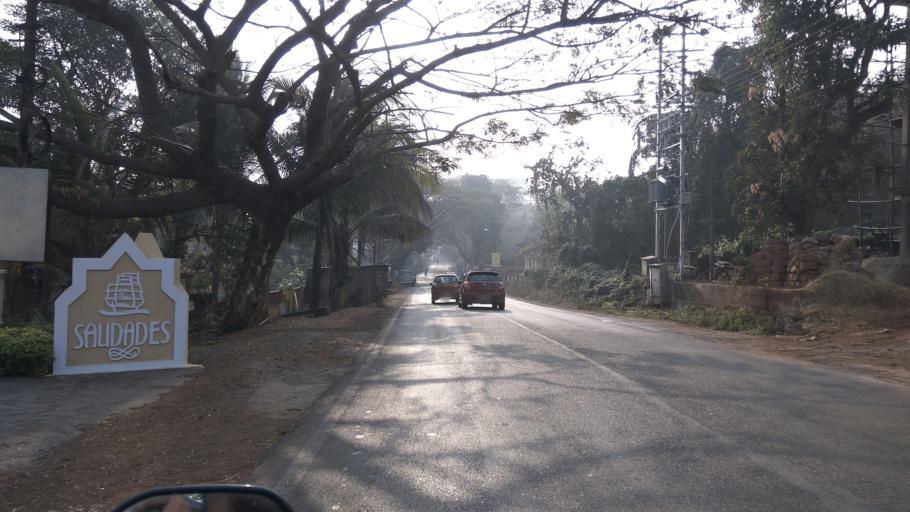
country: IN
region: Goa
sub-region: North Goa
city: Saligao
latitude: 15.5447
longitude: 73.8062
